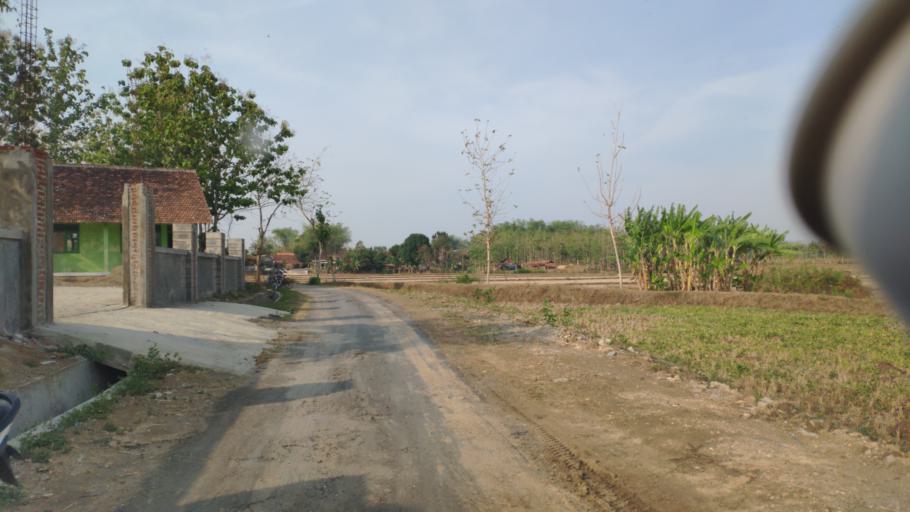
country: ID
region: Central Java
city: Weru
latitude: -6.9491
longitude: 111.4205
